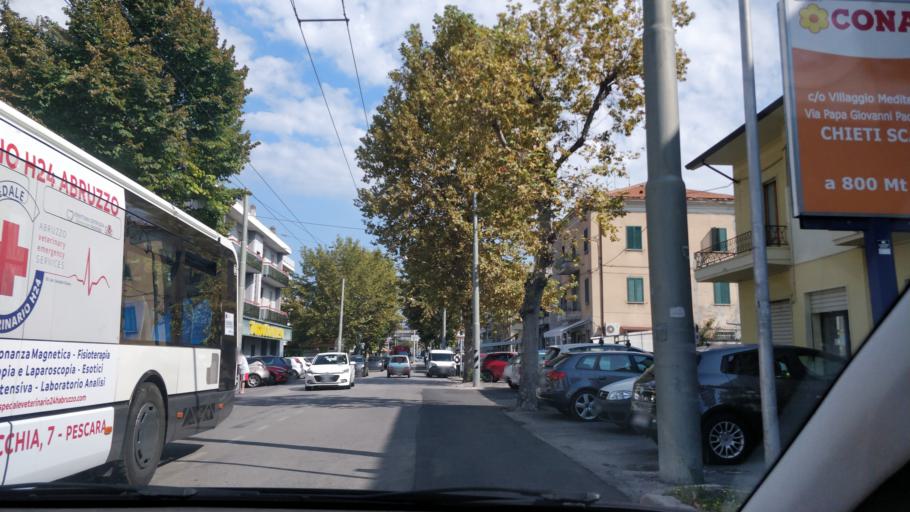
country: IT
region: Abruzzo
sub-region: Provincia di Chieti
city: Chieti
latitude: 42.3708
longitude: 14.1432
